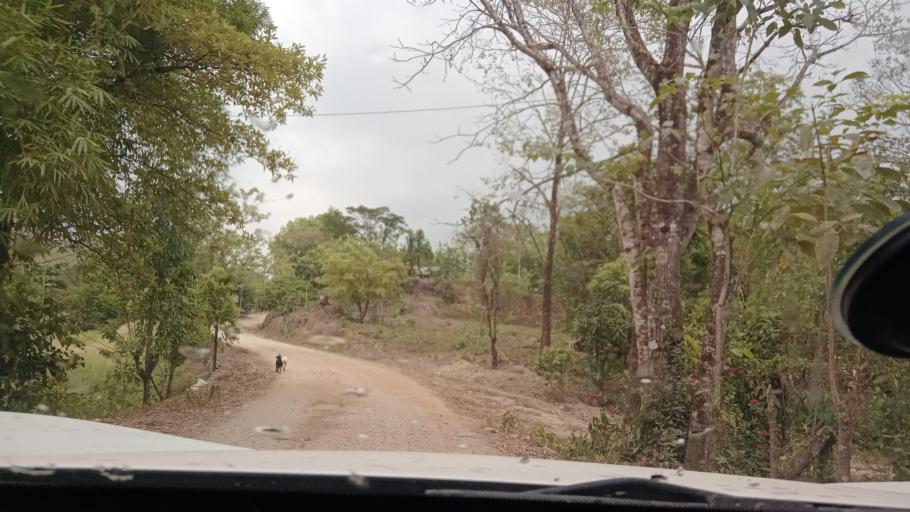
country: MX
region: Veracruz
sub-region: Uxpanapa
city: Poblado 10
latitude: 17.4518
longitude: -94.0938
